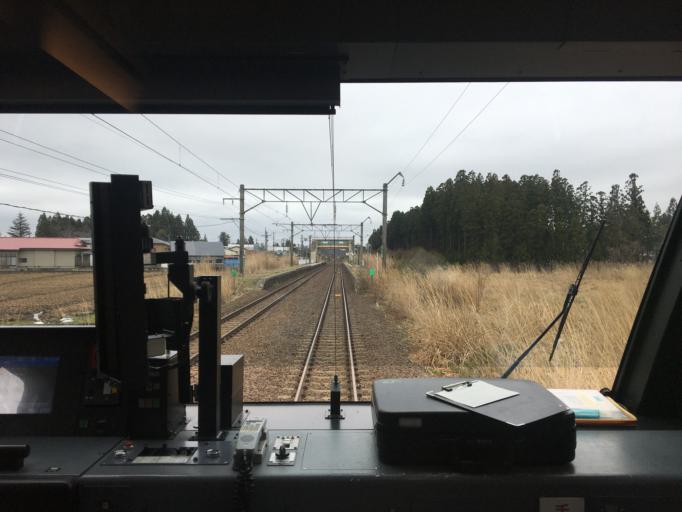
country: JP
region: Akita
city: Noshiromachi
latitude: 40.1428
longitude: 140.0630
